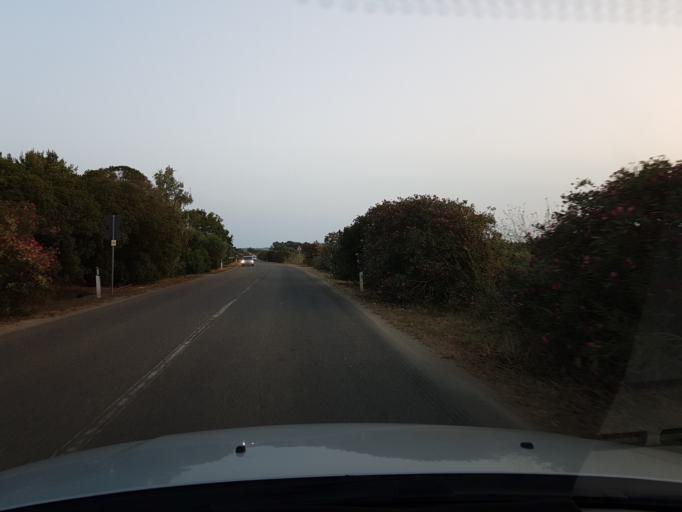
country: IT
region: Sardinia
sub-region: Provincia di Oristano
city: Cabras
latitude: 39.9248
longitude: 8.4540
